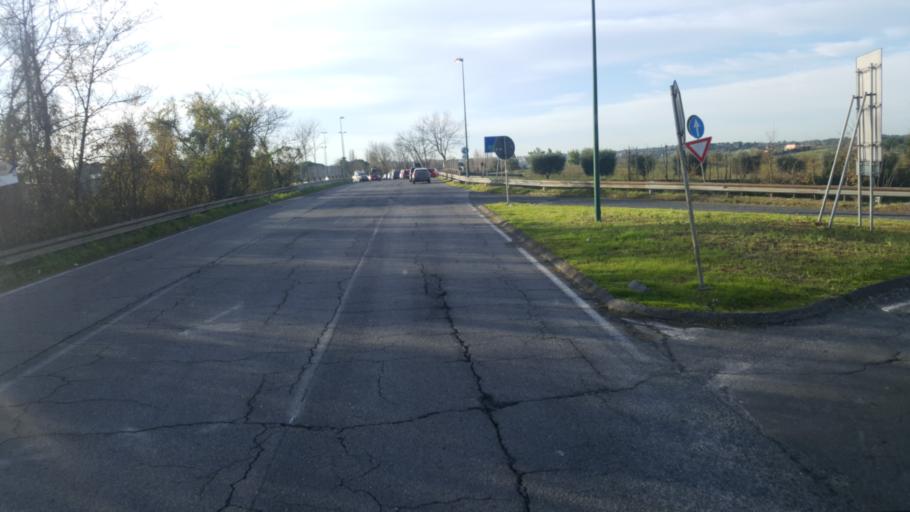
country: IT
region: Latium
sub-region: Citta metropolitana di Roma Capitale
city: Formello
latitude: 42.0462
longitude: 12.3951
